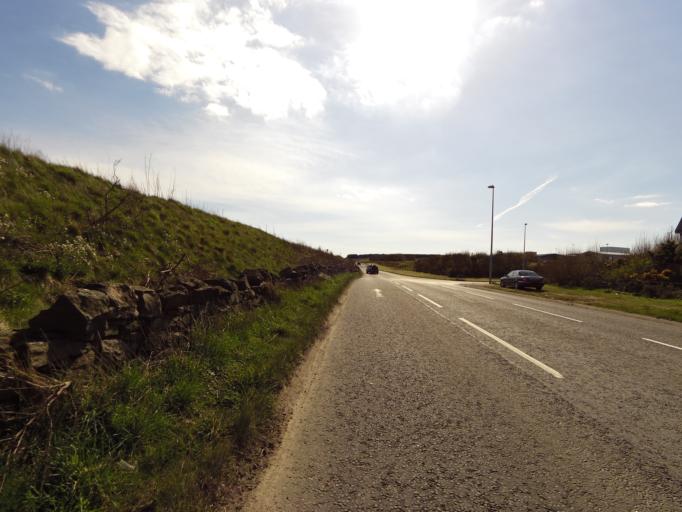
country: GB
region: Scotland
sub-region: Aberdeen City
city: Aberdeen
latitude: 57.1165
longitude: -2.0629
